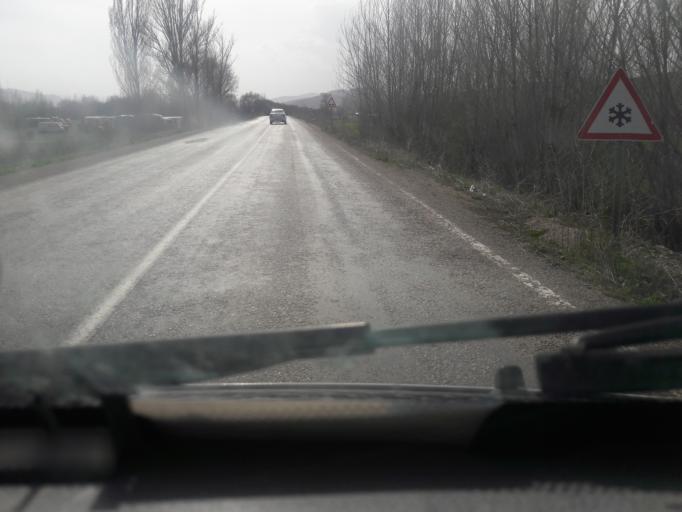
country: TR
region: Gumushane
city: Kelkit
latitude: 40.1429
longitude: 39.4270
